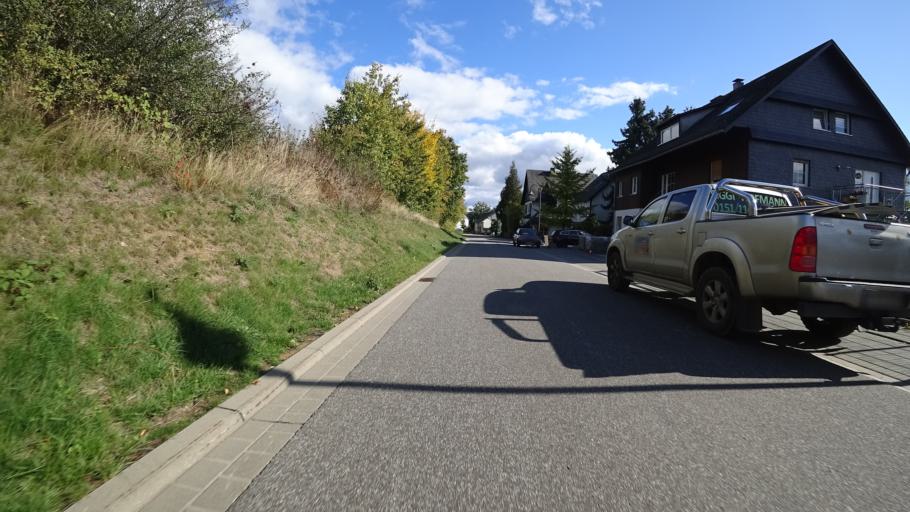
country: DE
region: Rheinland-Pfalz
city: Klosterkumbd
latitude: 50.0279
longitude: 7.5303
